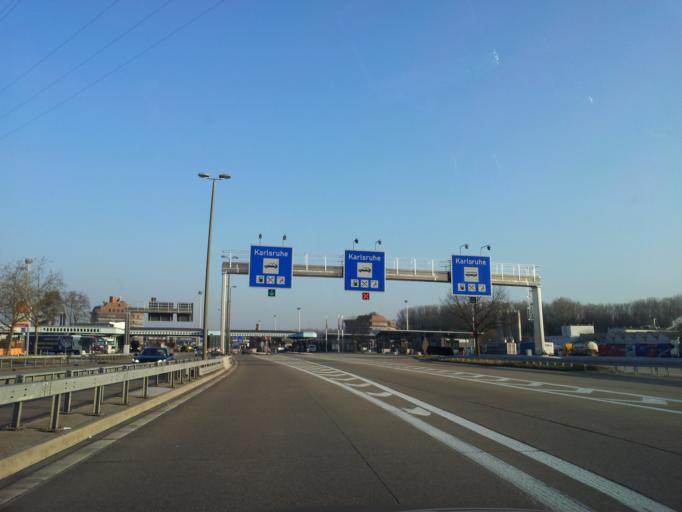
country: DE
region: Baden-Wuerttemberg
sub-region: Freiburg Region
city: Weil am Rhein
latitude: 47.5946
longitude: 7.6040
